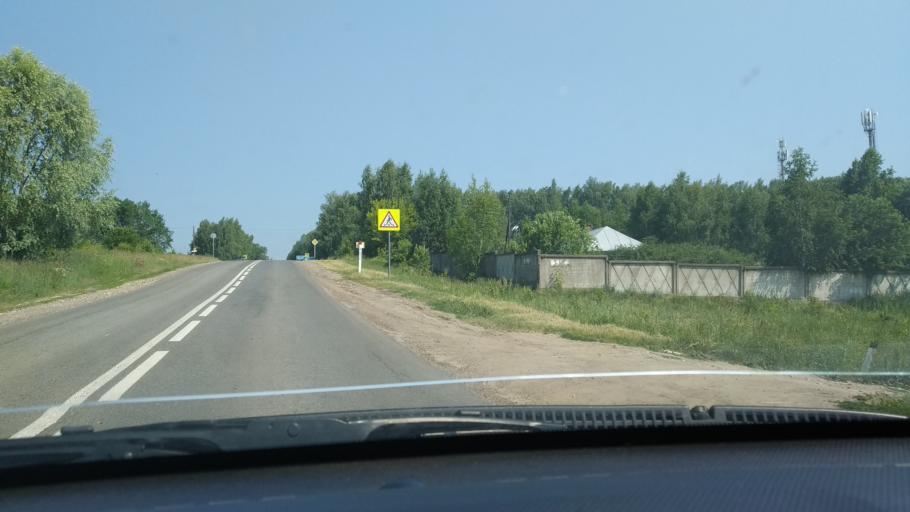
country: RU
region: Tatarstan
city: Osinovo
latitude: 55.9876
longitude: 48.8136
